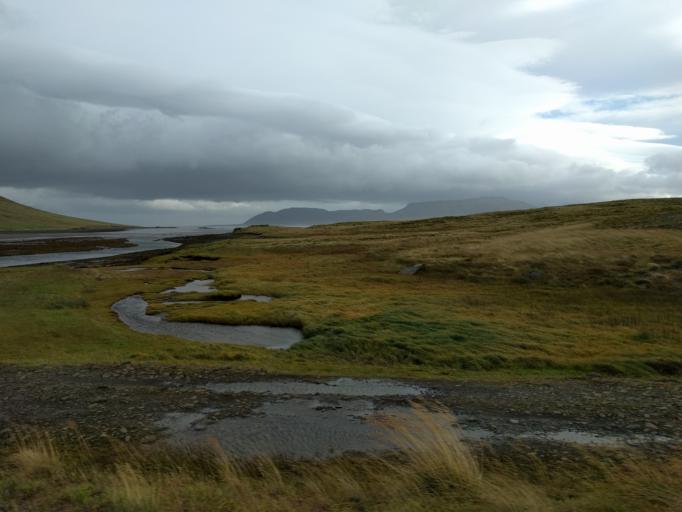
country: IS
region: West
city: Olafsvik
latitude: 64.9256
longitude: -23.3021
